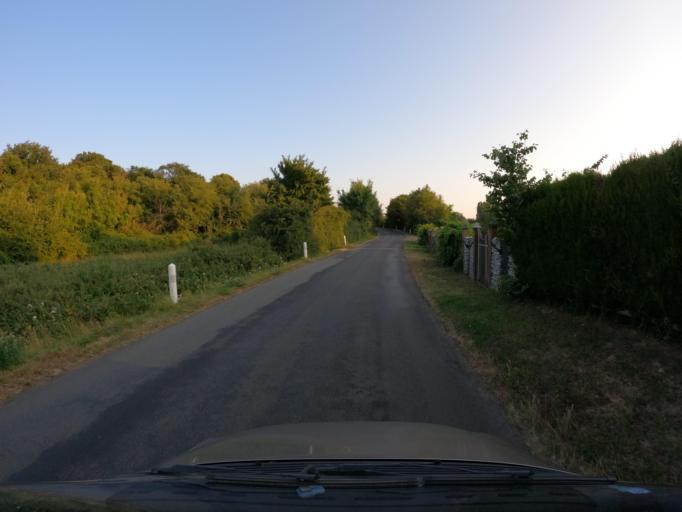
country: FR
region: Pays de la Loire
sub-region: Departement de la Sarthe
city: Parce-sur-Sarthe
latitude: 47.8520
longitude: -0.1934
